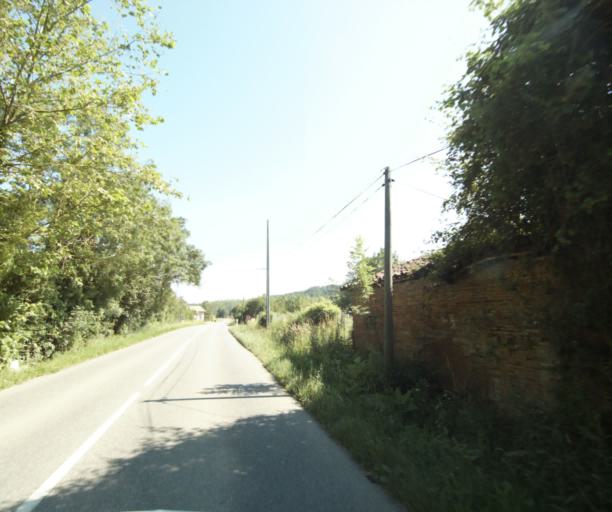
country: FR
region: Midi-Pyrenees
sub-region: Departement du Tarn-et-Garonne
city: Bressols
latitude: 43.9712
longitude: 1.3575
